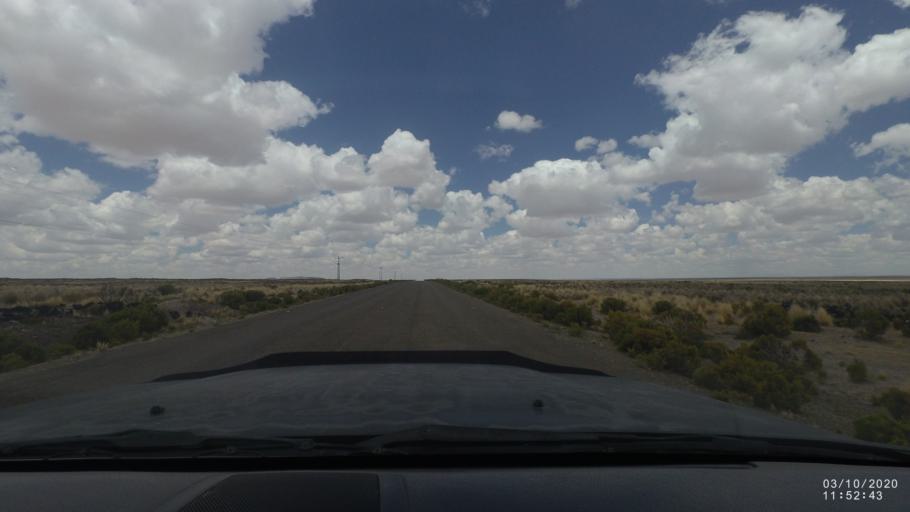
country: BO
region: Oruro
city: Poopo
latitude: -18.4654
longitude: -67.6009
